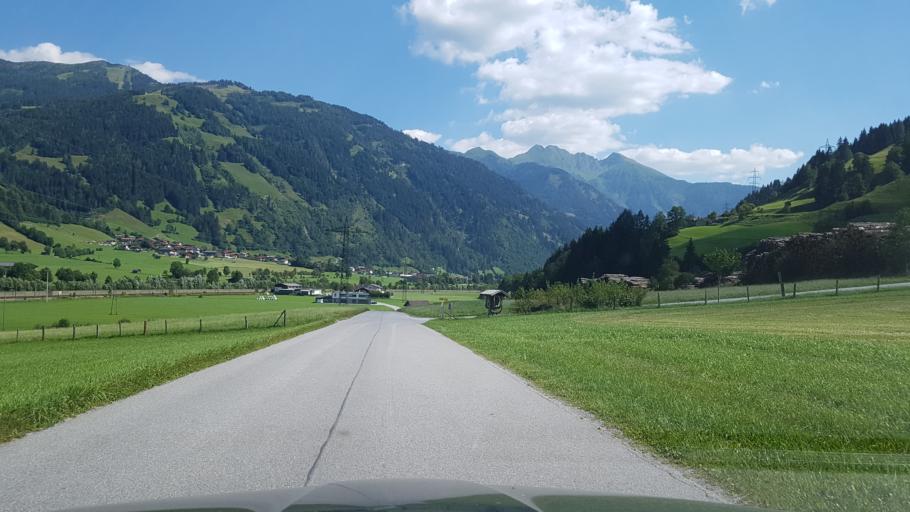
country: AT
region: Salzburg
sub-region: Politischer Bezirk Sankt Johann im Pongau
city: Dorfgastein
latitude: 47.2532
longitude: 13.0923
